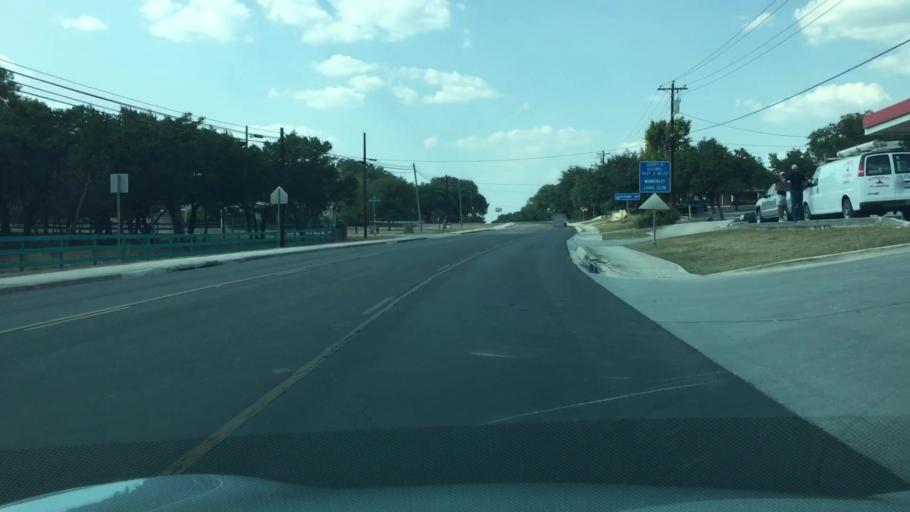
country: US
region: Texas
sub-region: Hays County
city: Wimberley
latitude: 30.0044
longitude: -98.1024
